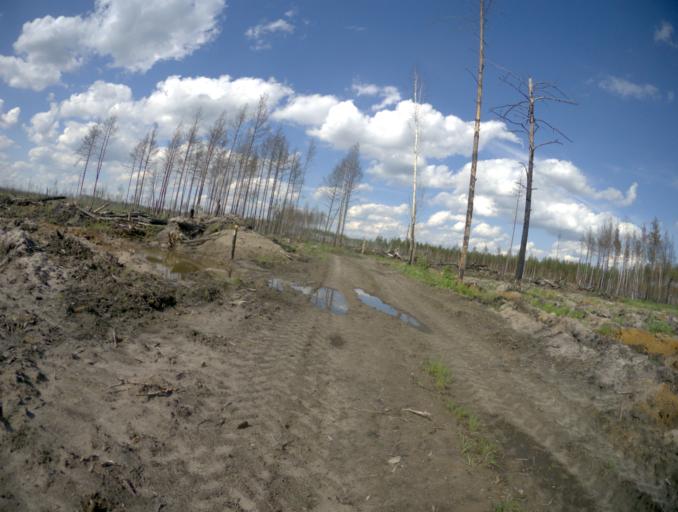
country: RU
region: Vladimir
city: Velikodvorskiy
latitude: 55.3144
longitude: 40.9180
